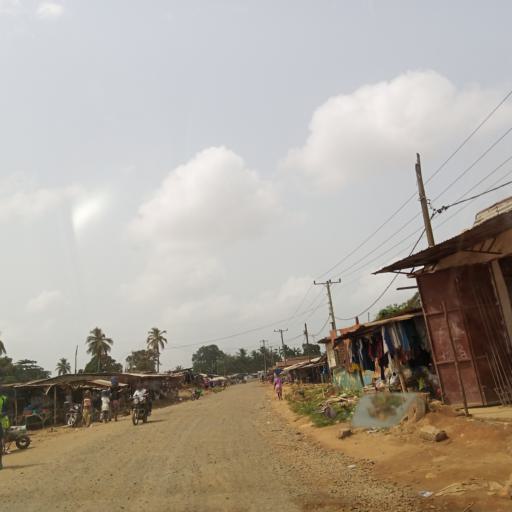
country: LR
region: Montserrado
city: Monrovia
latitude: 6.3478
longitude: -10.7321
